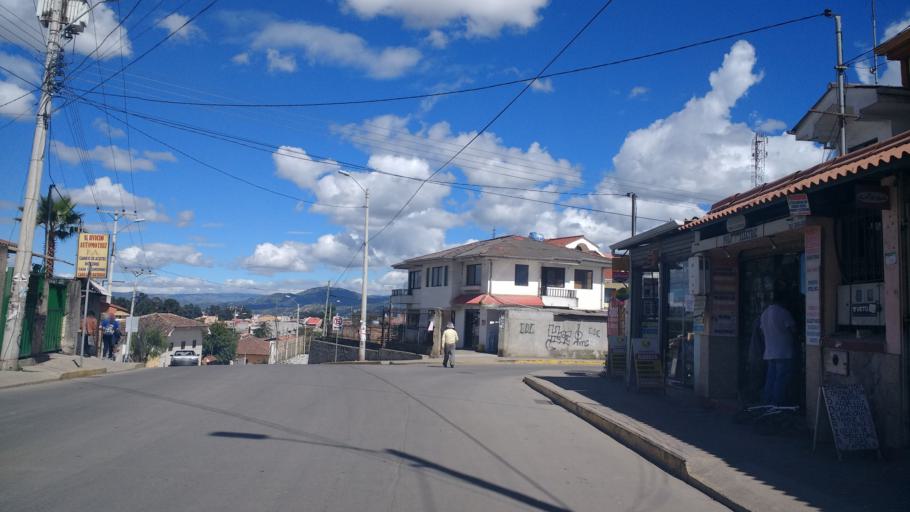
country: EC
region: Azuay
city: Cuenca
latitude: -2.8956
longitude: -79.0354
